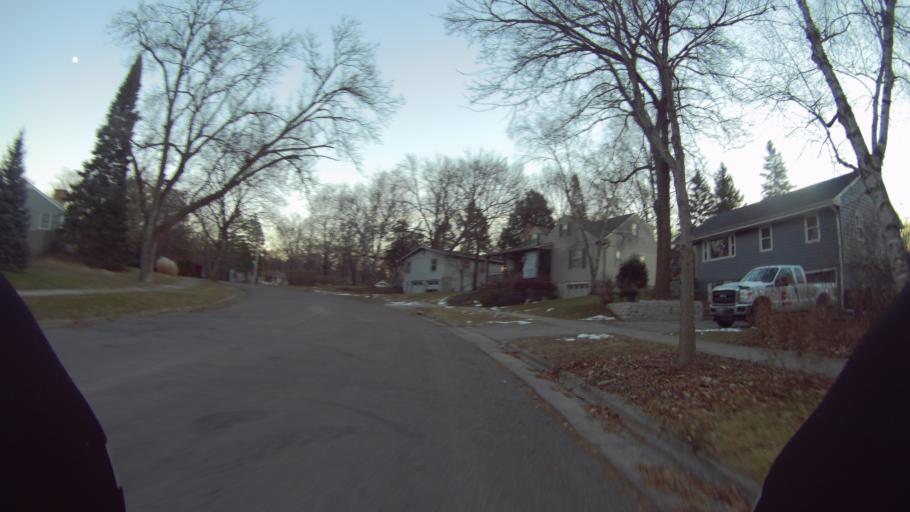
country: US
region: Wisconsin
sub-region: Dane County
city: Shorewood Hills
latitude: 43.0639
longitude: -89.4530
